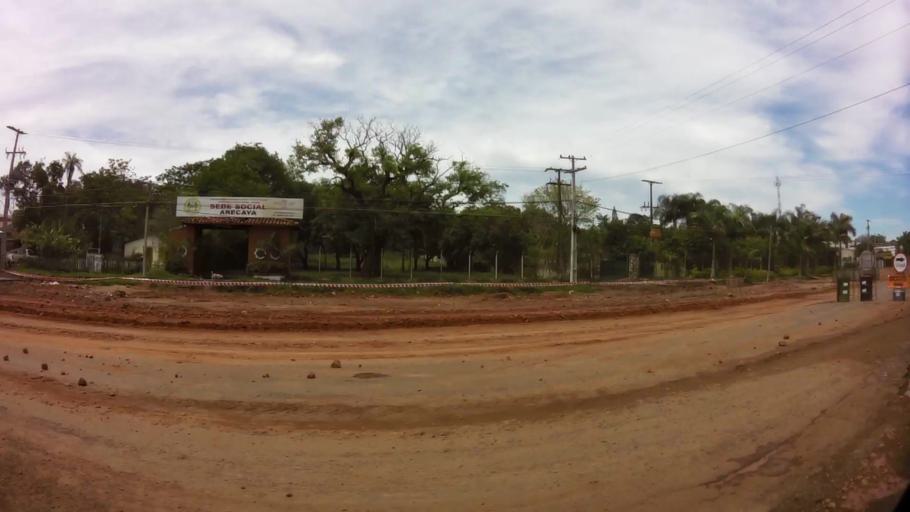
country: PY
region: Central
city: Limpio
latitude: -25.1964
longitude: -57.5134
